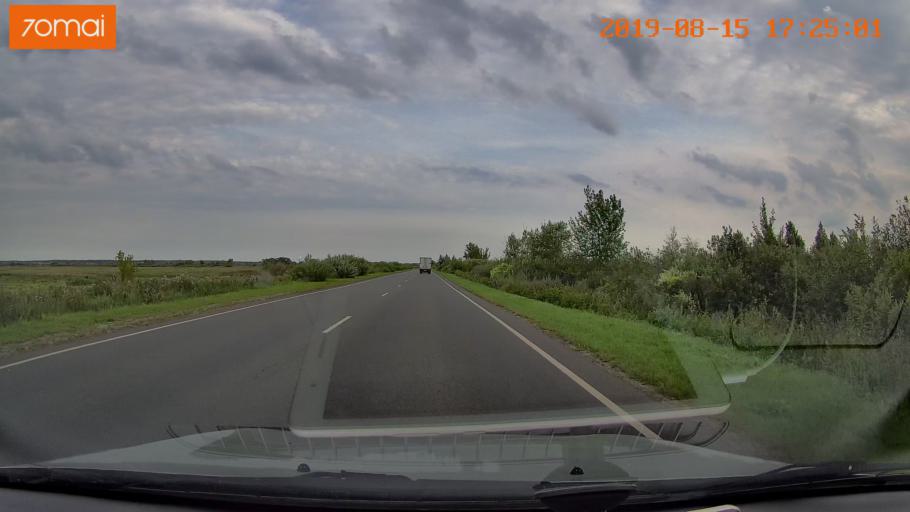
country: RU
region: Moskovskaya
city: Ashitkovo
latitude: 55.3794
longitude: 38.5602
